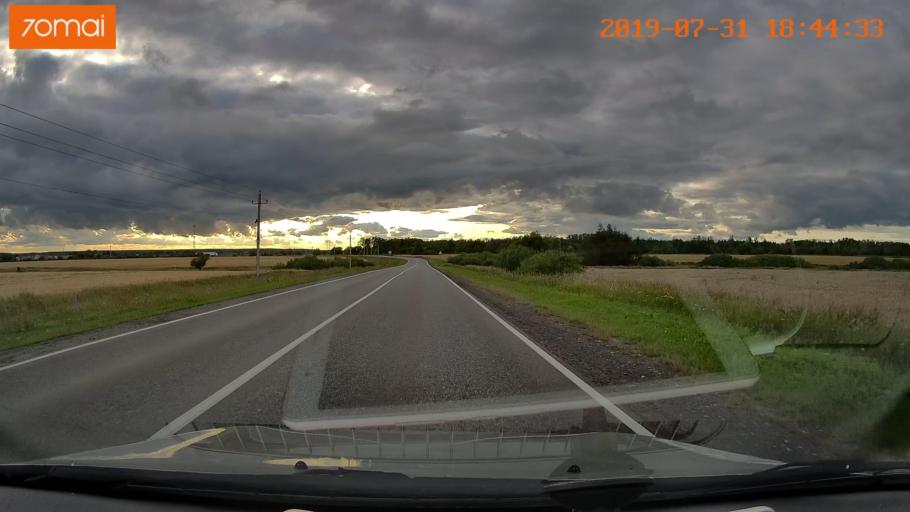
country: RU
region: Moskovskaya
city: Troitskoye
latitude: 55.2507
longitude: 38.5495
